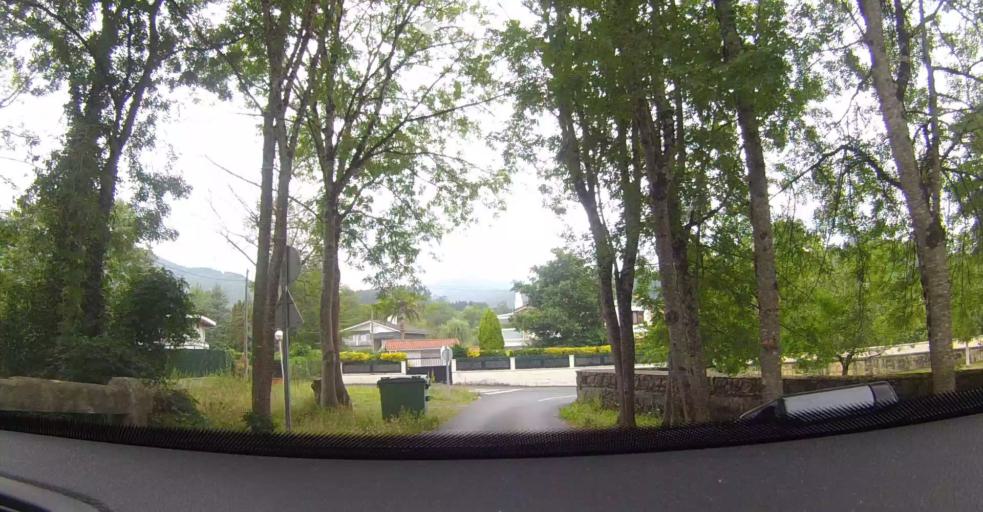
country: ES
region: Basque Country
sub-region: Bizkaia
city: Sopuerta
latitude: 43.2597
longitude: -3.1514
